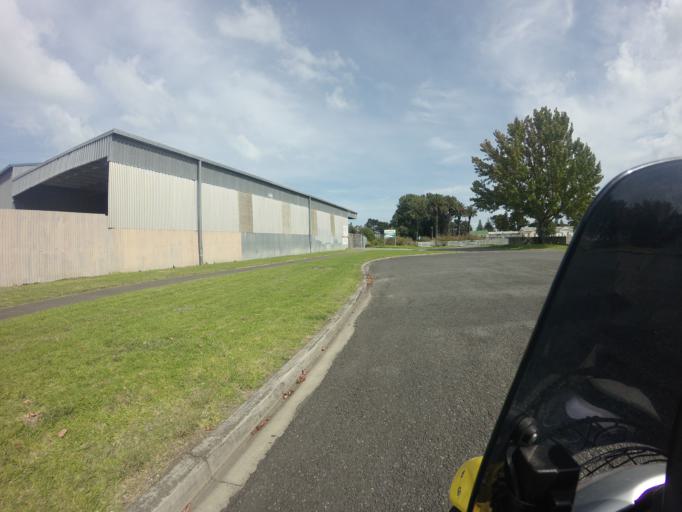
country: NZ
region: Gisborne
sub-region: Gisborne District
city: Gisborne
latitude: -38.6693
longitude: 178.0226
